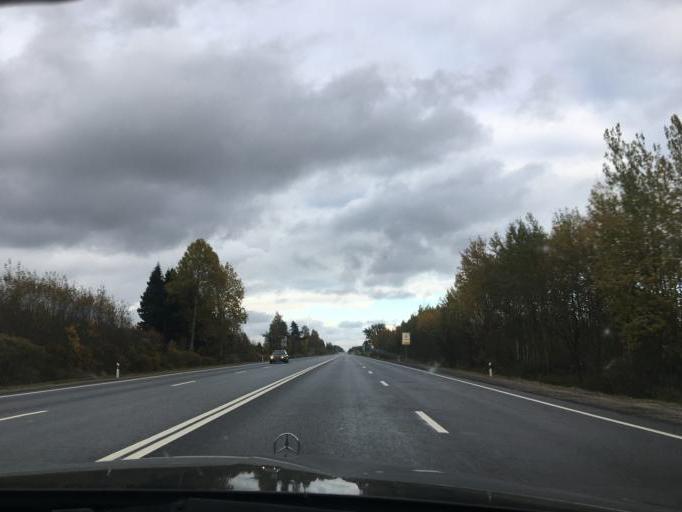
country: RU
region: Smolensk
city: Rudnya
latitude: 54.6940
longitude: 31.1045
